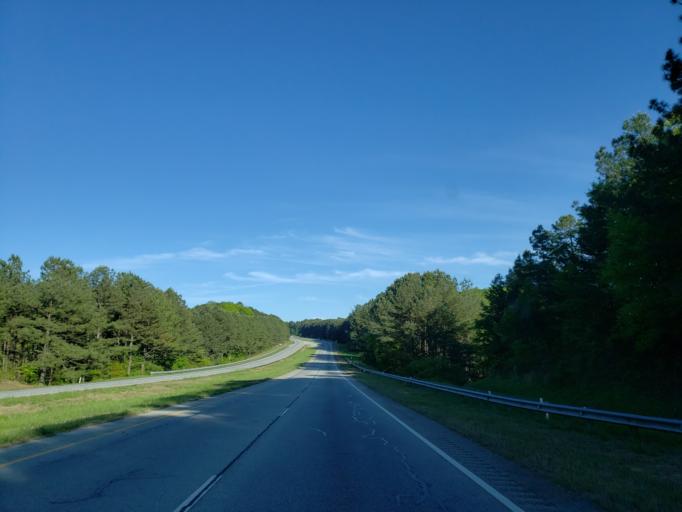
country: US
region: Georgia
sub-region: Polk County
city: Rockmart
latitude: 33.9322
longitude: -84.9622
